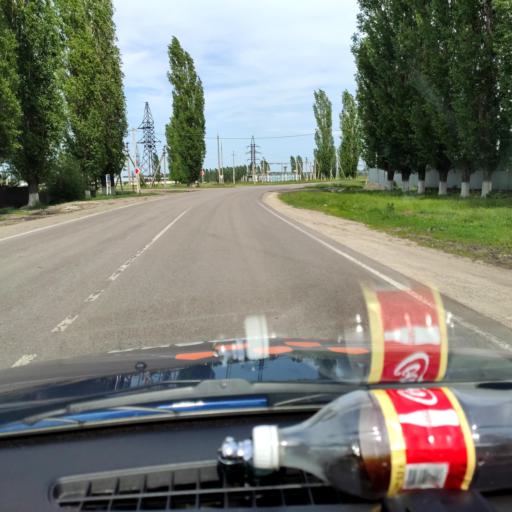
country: RU
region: Voronezj
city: Novaya Usman'
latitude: 51.5442
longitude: 39.3539
